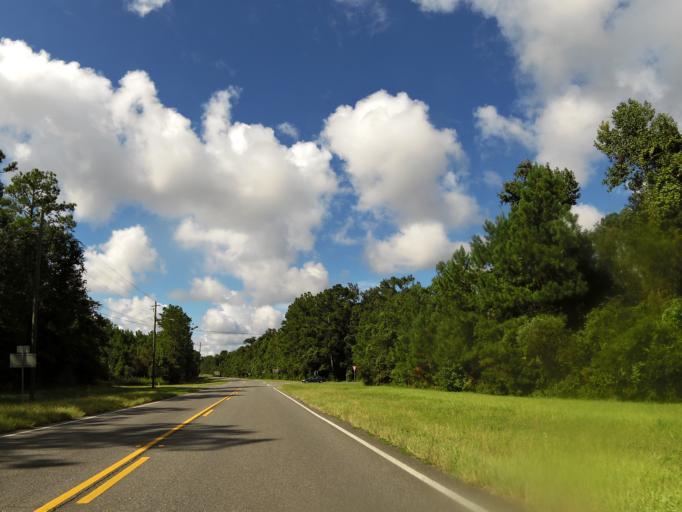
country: US
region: Georgia
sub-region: Camden County
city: Kingsland
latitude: 30.7797
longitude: -81.6867
